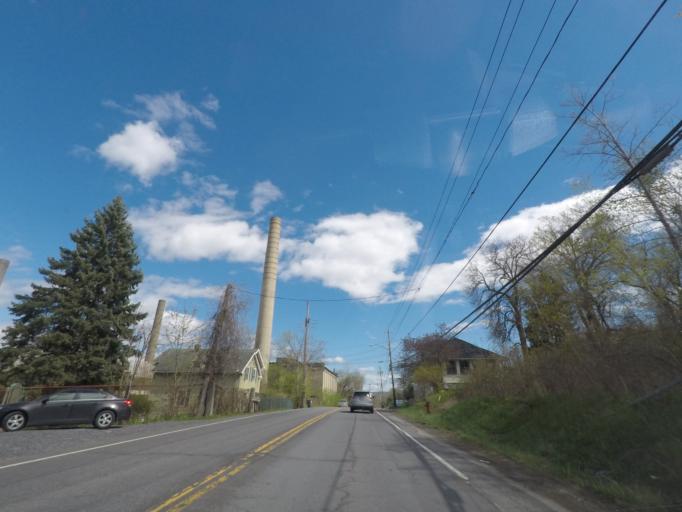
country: US
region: New York
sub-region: Columbia County
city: Oakdale
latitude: 42.2404
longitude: -73.7615
